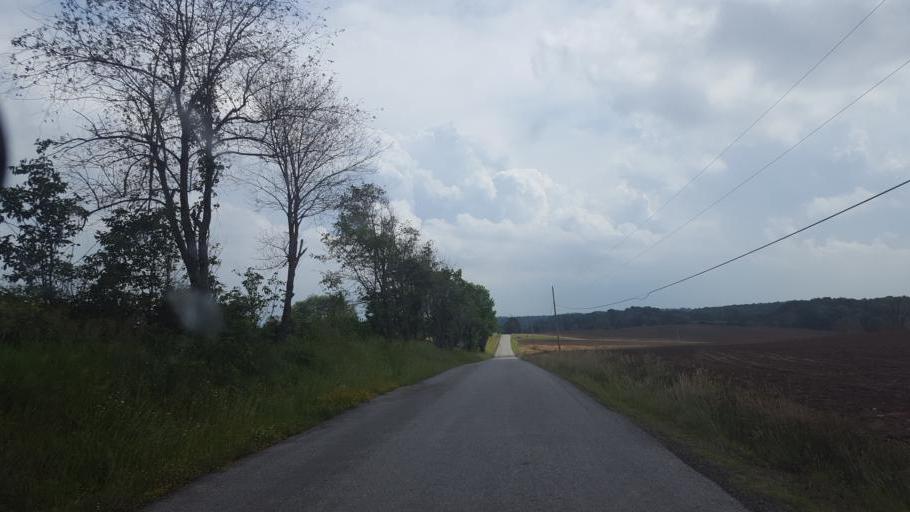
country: US
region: Ohio
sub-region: Knox County
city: Oak Hill
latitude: 40.2916
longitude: -82.1829
